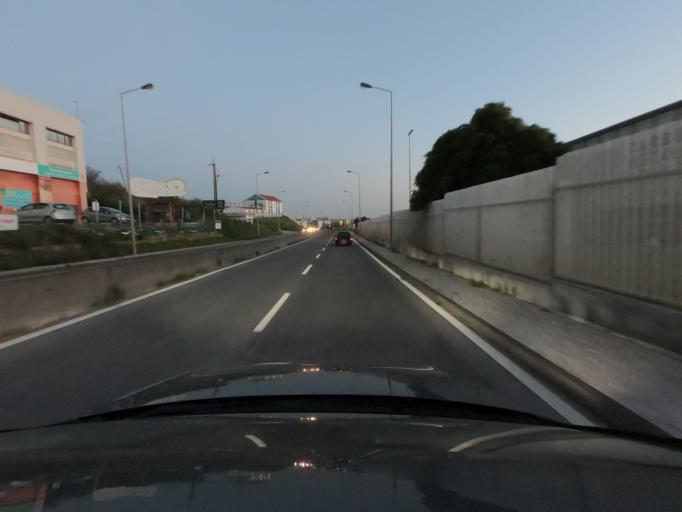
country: PT
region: Lisbon
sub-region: Sintra
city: Cacem
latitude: 38.7539
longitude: -9.3069
